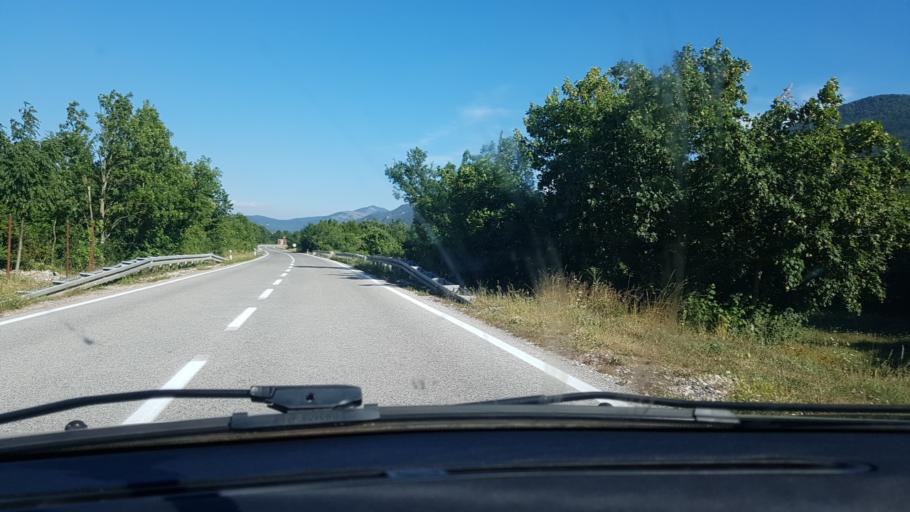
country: HR
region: Zadarska
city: Gracac
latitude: 44.2985
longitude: 15.8313
